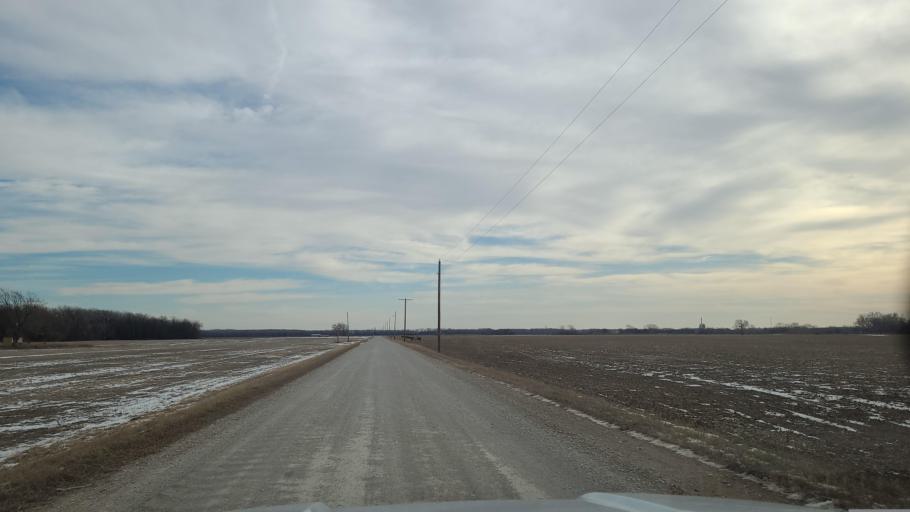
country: US
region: Kansas
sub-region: Douglas County
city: Lawrence
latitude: 39.0297
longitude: -95.3259
